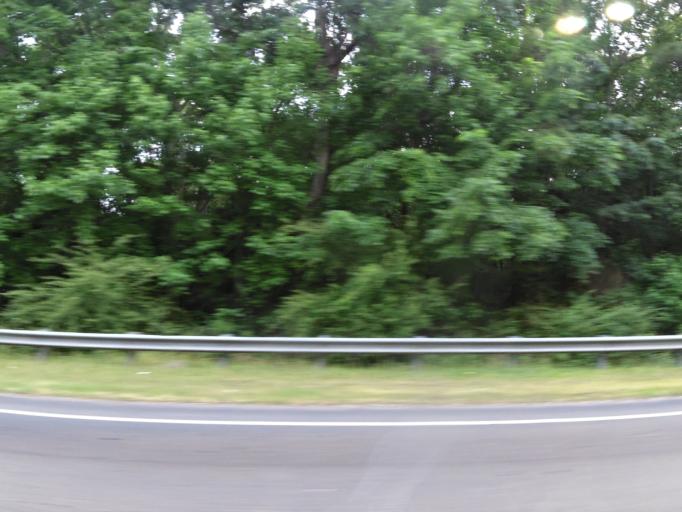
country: US
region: Georgia
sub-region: Chatham County
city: Pooler
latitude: 32.0955
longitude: -81.2098
